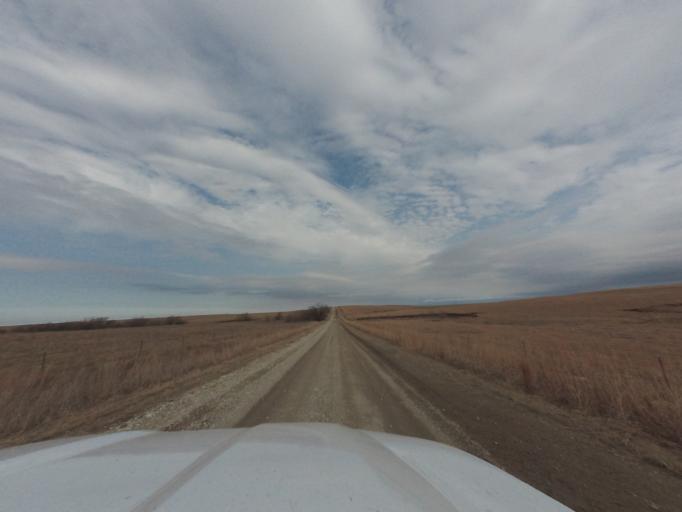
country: US
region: Kansas
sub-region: Chase County
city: Cottonwood Falls
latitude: 38.2245
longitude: -96.7307
